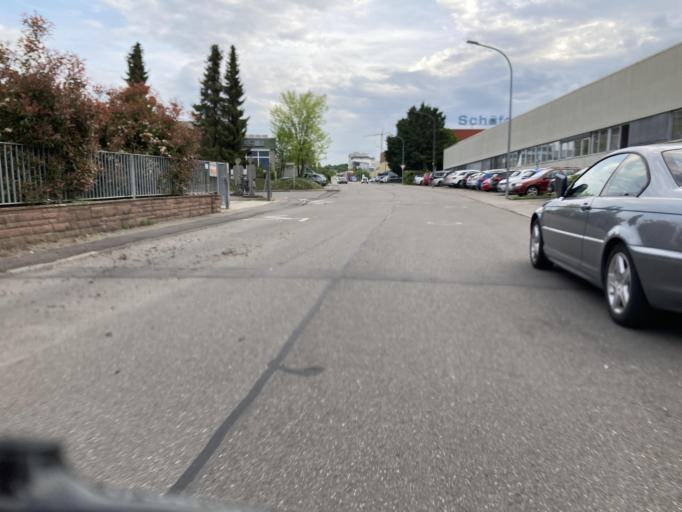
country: DE
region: Baden-Wuerttemberg
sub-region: Regierungsbezirk Stuttgart
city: Renningen
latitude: 48.7763
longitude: 8.9261
